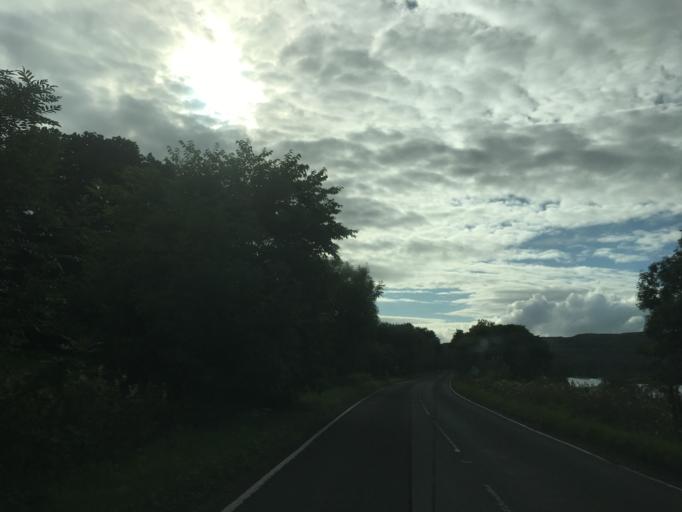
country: GB
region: Scotland
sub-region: Argyll and Bute
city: Oban
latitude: 56.3523
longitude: -5.4801
